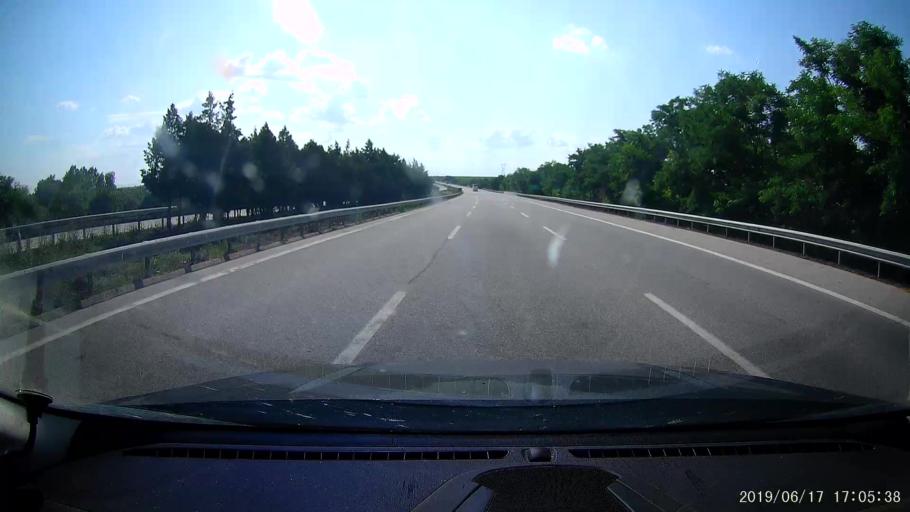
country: TR
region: Edirne
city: Edirne
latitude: 41.6611
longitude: 26.6940
